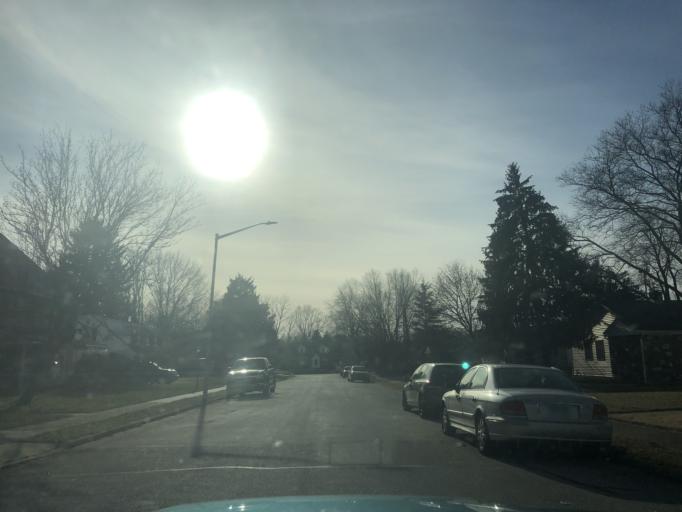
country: US
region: Pennsylvania
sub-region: Montgomery County
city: Flourtown
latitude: 40.1143
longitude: -75.1986
